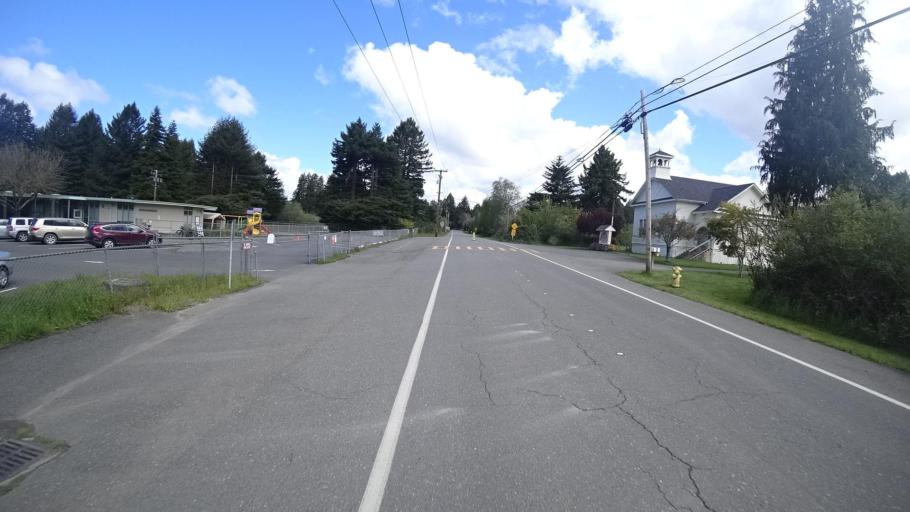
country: US
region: California
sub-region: Humboldt County
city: McKinleyville
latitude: 40.9563
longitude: -124.0337
